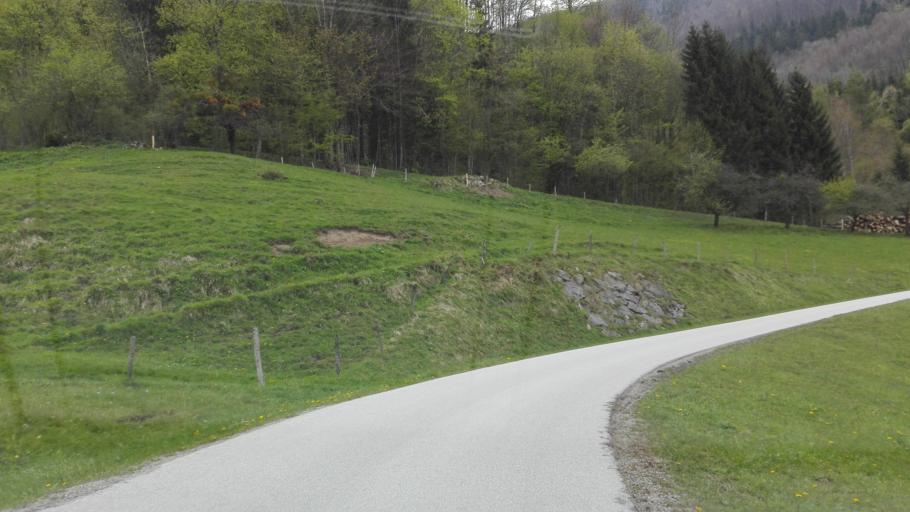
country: AT
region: Upper Austria
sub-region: Politischer Bezirk Steyr-Land
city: Ternberg
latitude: 47.9212
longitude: 14.3233
